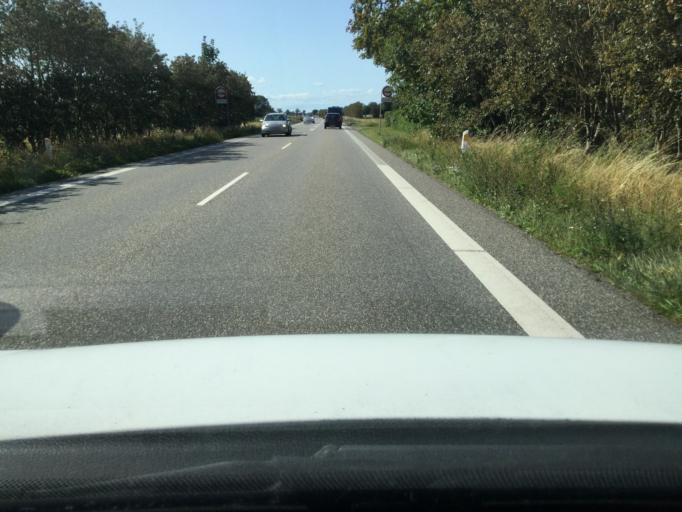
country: DK
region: Zealand
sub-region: Lolland Kommune
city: Nakskov
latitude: 54.8032
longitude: 11.2460
